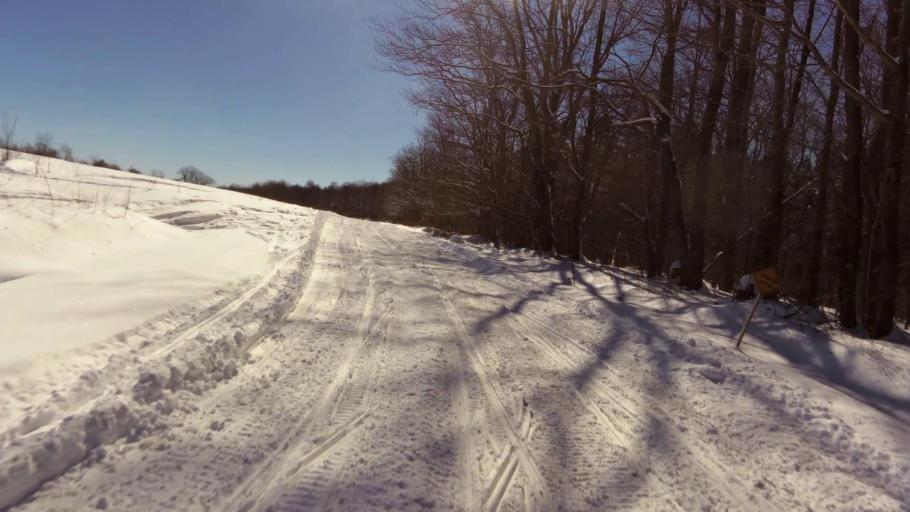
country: US
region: New York
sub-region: Chautauqua County
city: Mayville
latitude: 42.2175
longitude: -79.5347
